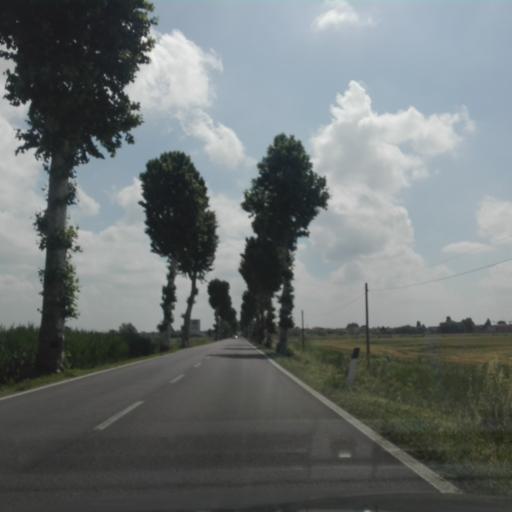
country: IT
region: Veneto
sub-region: Provincia di Rovigo
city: Buso
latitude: 45.0744
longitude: 11.8708
